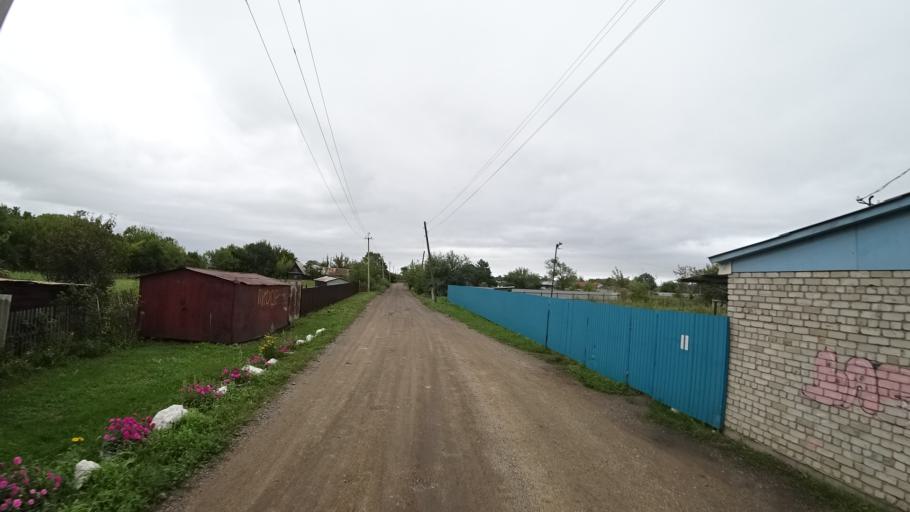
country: RU
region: Primorskiy
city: Chernigovka
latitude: 44.3355
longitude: 132.5332
